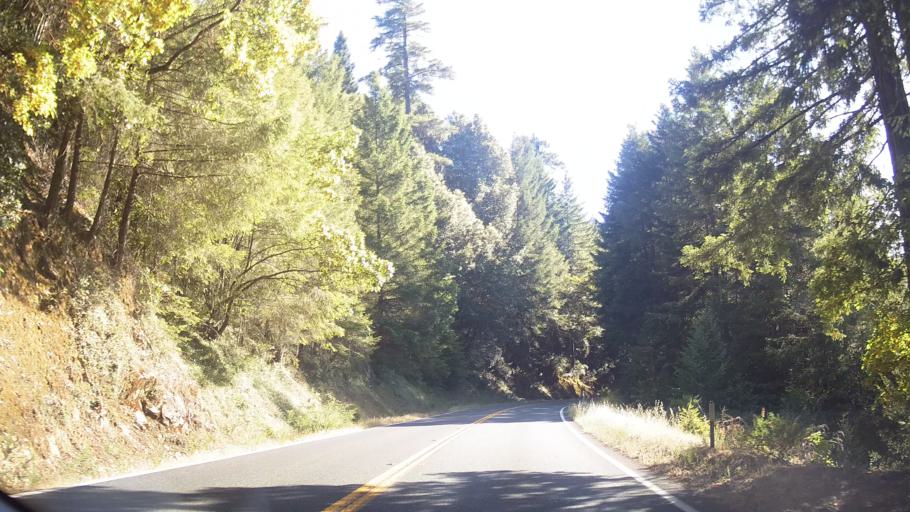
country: US
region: California
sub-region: Mendocino County
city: Brooktrails
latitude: 39.3864
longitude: -123.4696
